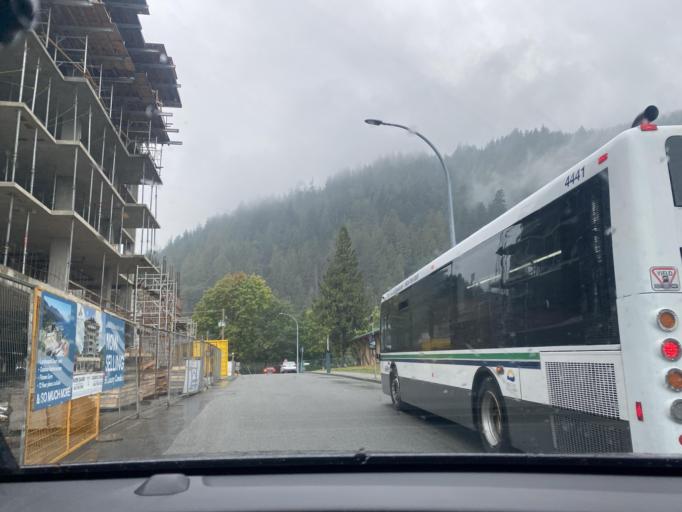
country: CA
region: British Columbia
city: Agassiz
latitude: 49.3036
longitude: -121.7878
